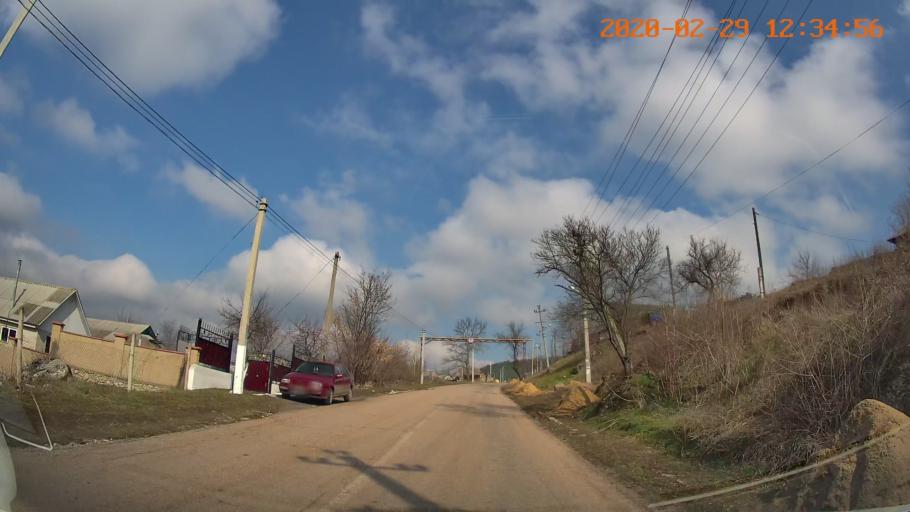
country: MD
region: Telenesti
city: Camenca
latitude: 48.0435
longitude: 28.7173
